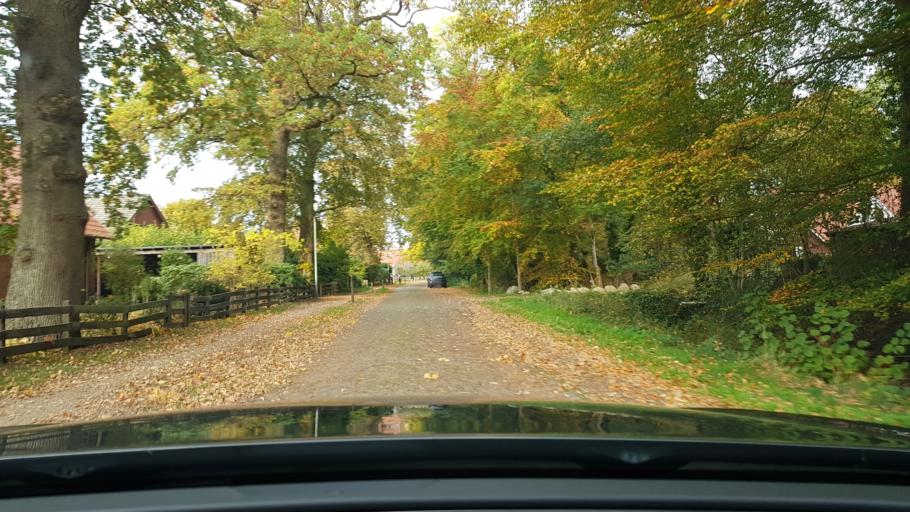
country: DE
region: Lower Saxony
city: Beverstedt
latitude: 53.4239
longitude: 8.8121
